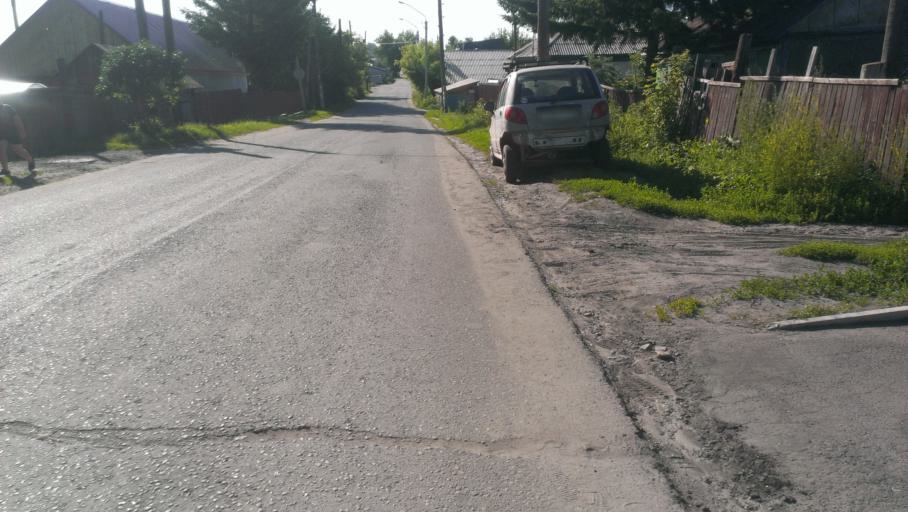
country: RU
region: Altai Krai
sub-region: Gorod Barnaulskiy
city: Barnaul
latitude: 53.3556
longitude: 83.7500
